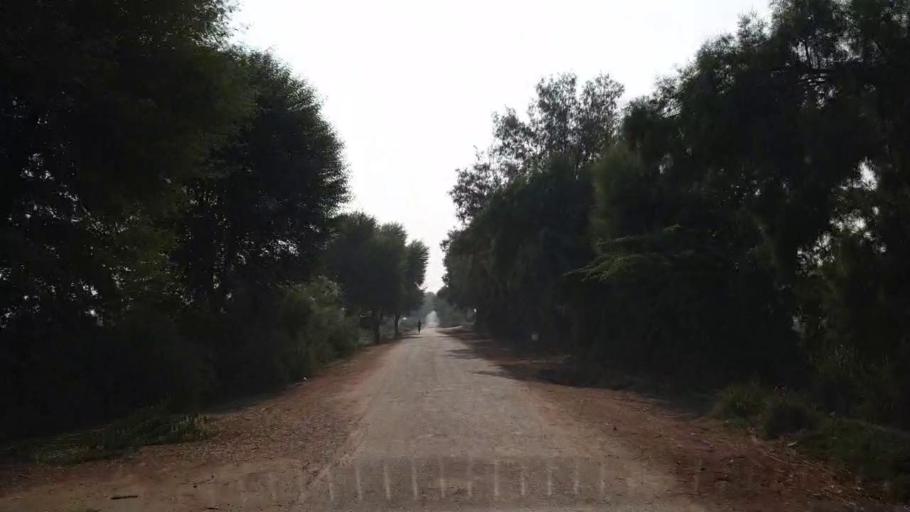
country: PK
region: Sindh
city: Bhan
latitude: 26.4740
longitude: 67.7738
